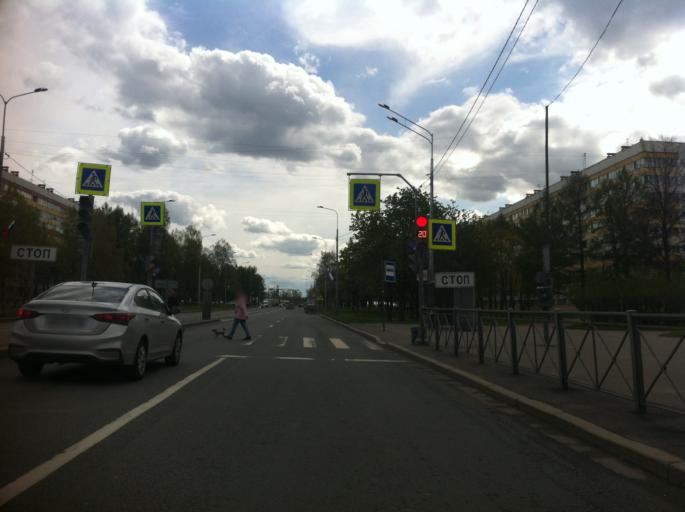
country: RU
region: St.-Petersburg
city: Uritsk
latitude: 59.8293
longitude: 30.1756
